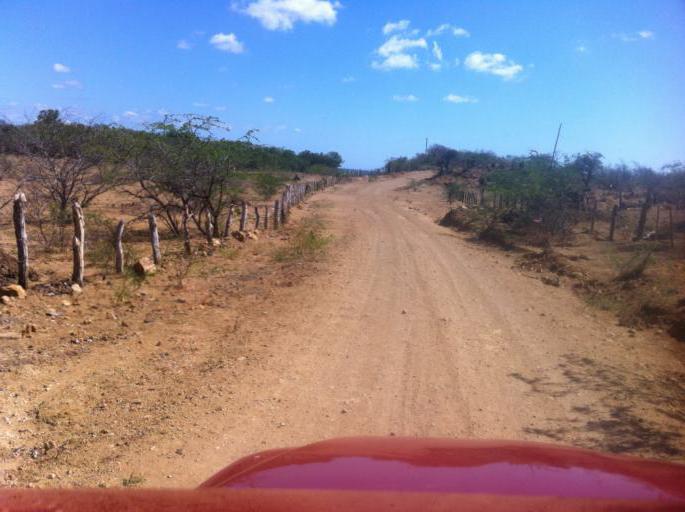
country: NI
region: Carazo
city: Santa Teresa
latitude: 11.6111
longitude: -86.3093
